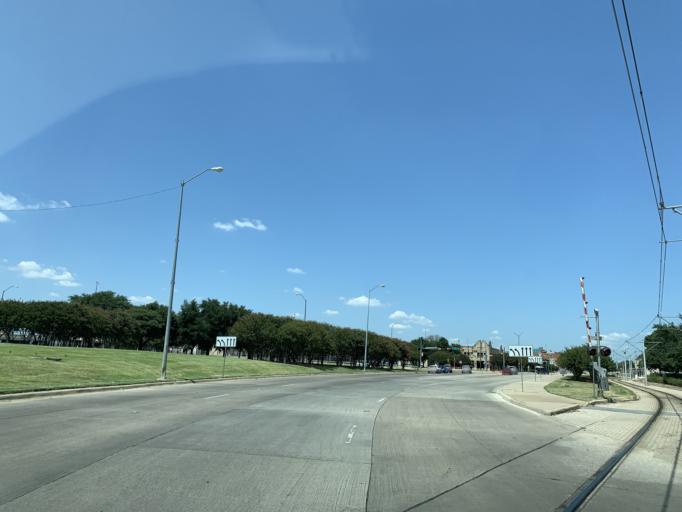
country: US
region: Texas
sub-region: Dallas County
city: Dallas
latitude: 32.7792
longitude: -96.7671
